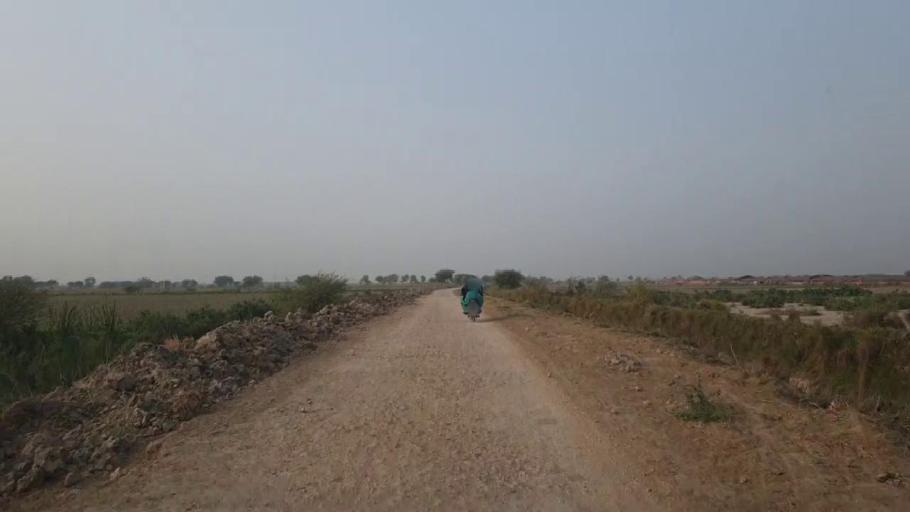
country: PK
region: Sindh
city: Mirpur Batoro
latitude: 24.6559
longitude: 68.3785
